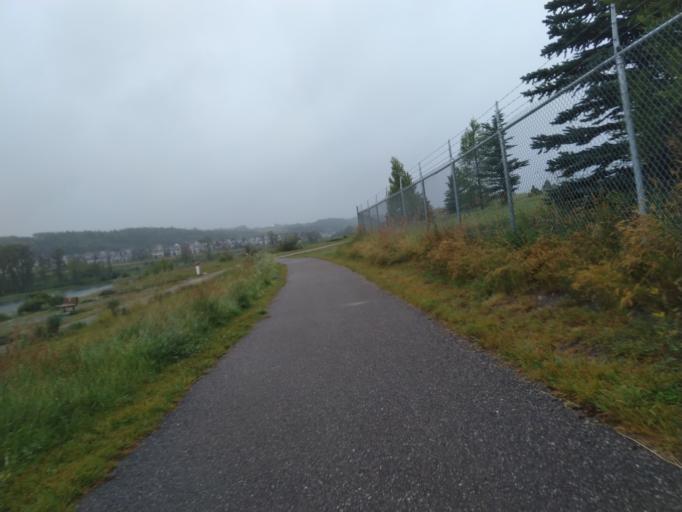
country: CA
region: Alberta
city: Cochrane
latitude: 51.1741
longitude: -114.4504
